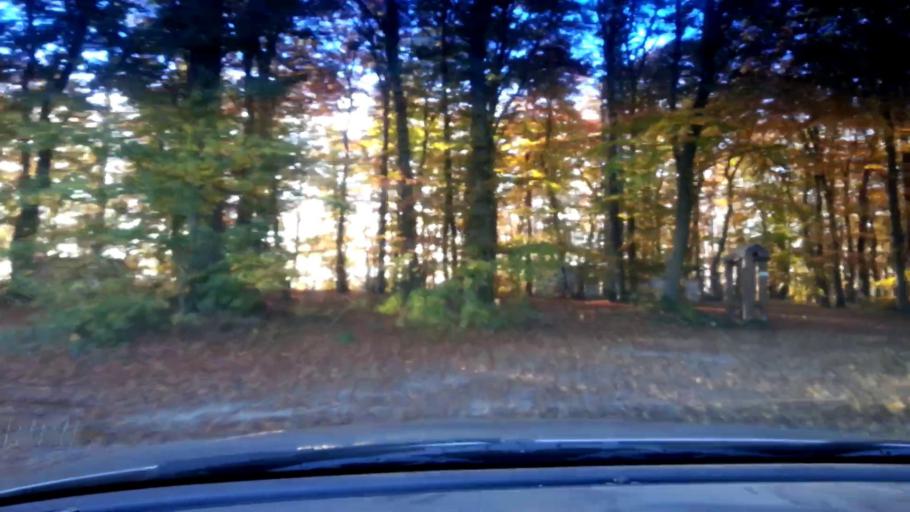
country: DE
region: Bavaria
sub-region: Upper Franconia
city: Heiligenstadt
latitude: 49.8624
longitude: 11.1833
